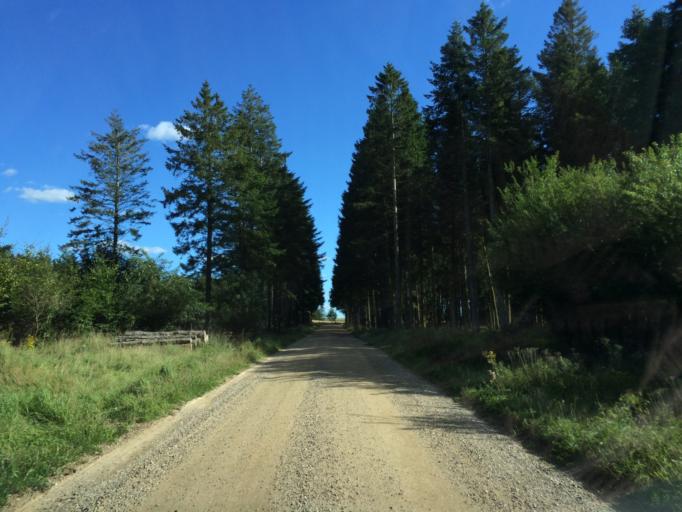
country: DK
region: Central Jutland
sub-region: Holstebro Kommune
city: Ulfborg
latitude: 56.2788
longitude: 8.4764
